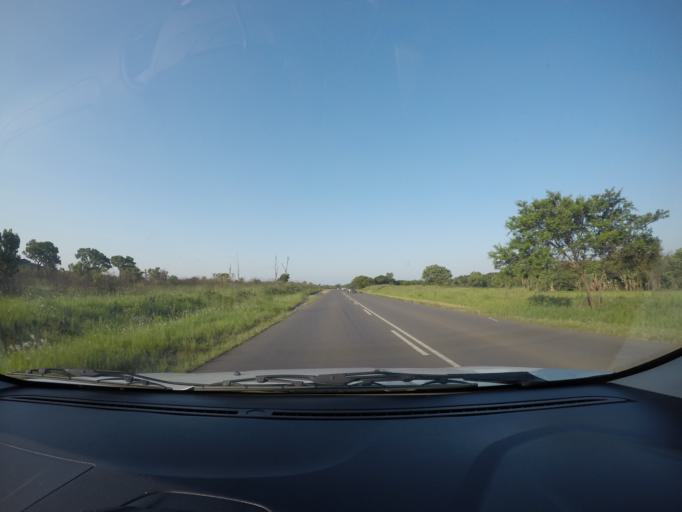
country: ZA
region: KwaZulu-Natal
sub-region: uThungulu District Municipality
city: Richards Bay
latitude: -28.7513
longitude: 32.0104
